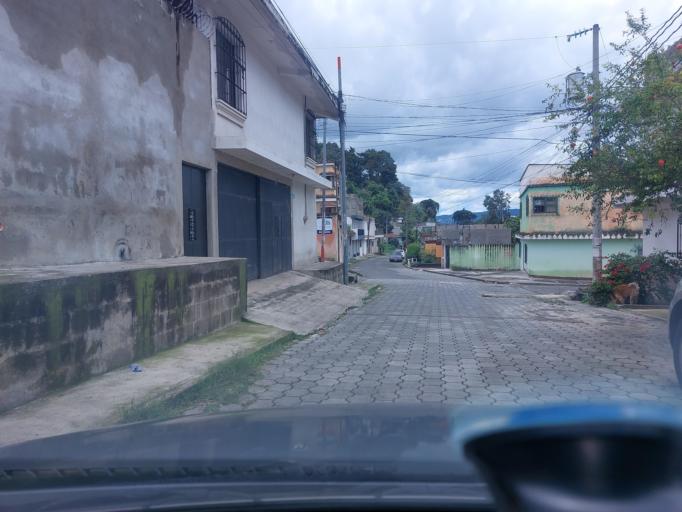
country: GT
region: Chimaltenango
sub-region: Municipio de Chimaltenango
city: Chimaltenango
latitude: 14.6560
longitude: -90.8198
